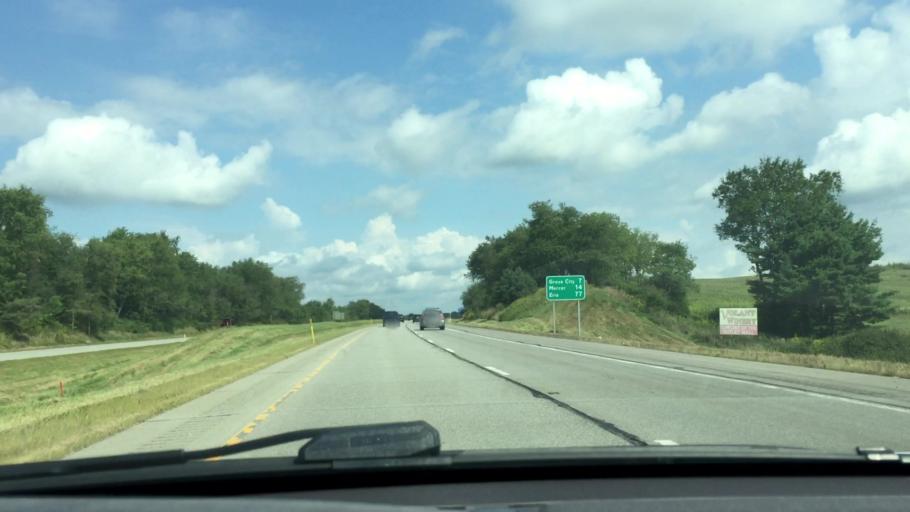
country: US
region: Pennsylvania
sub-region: Butler County
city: Slippery Rock
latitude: 41.0499
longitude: -80.1264
